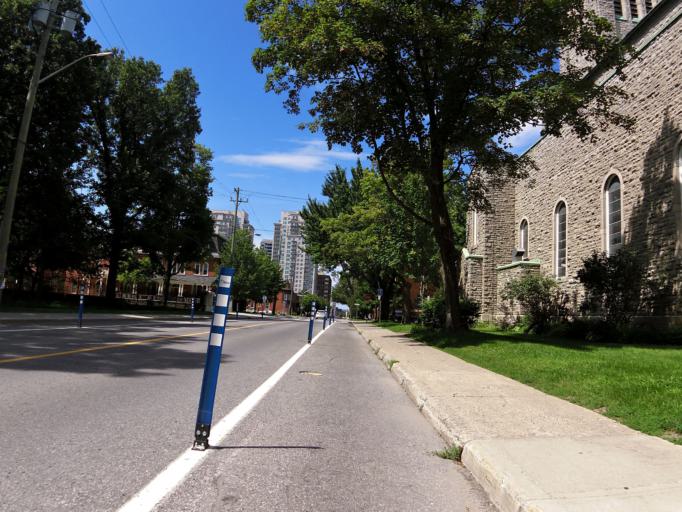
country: CA
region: Ontario
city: Ottawa
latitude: 45.4250
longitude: -75.6851
